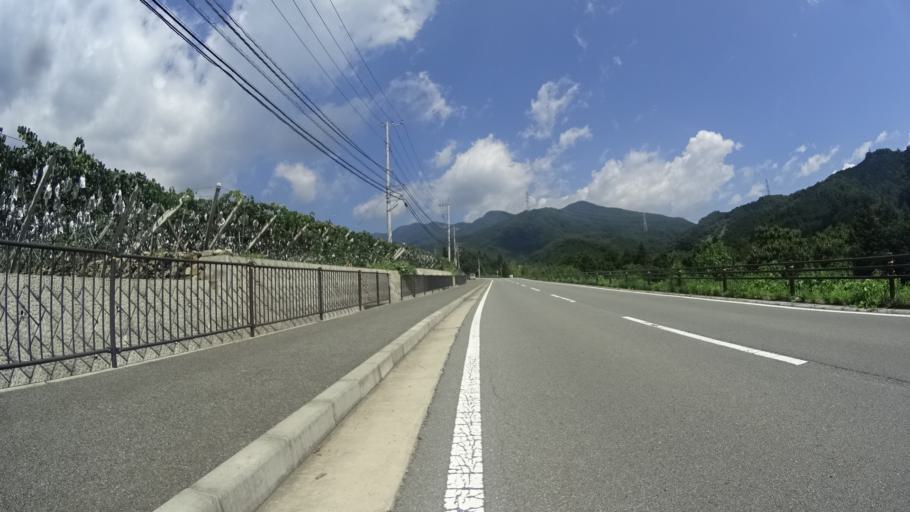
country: JP
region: Yamanashi
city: Enzan
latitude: 35.7594
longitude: 138.7063
